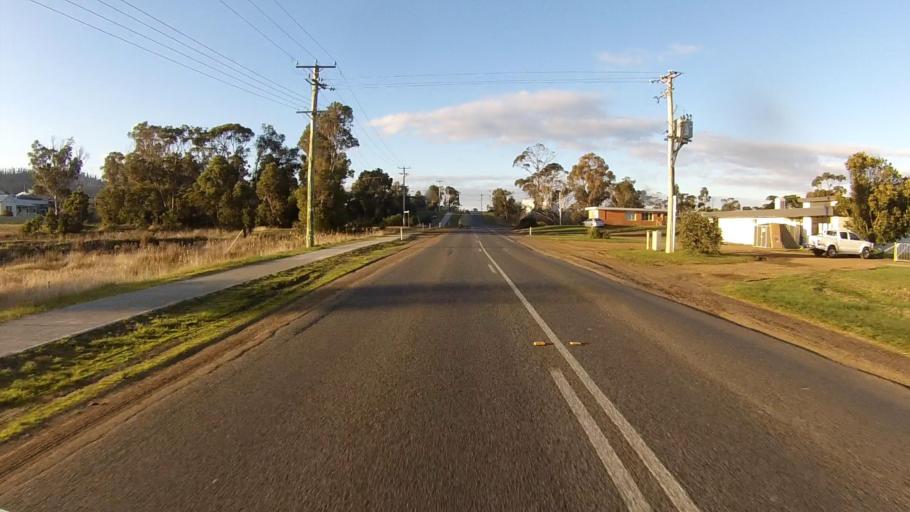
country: AU
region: Tasmania
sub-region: Sorell
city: Sorell
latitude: -42.8887
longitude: 147.8085
